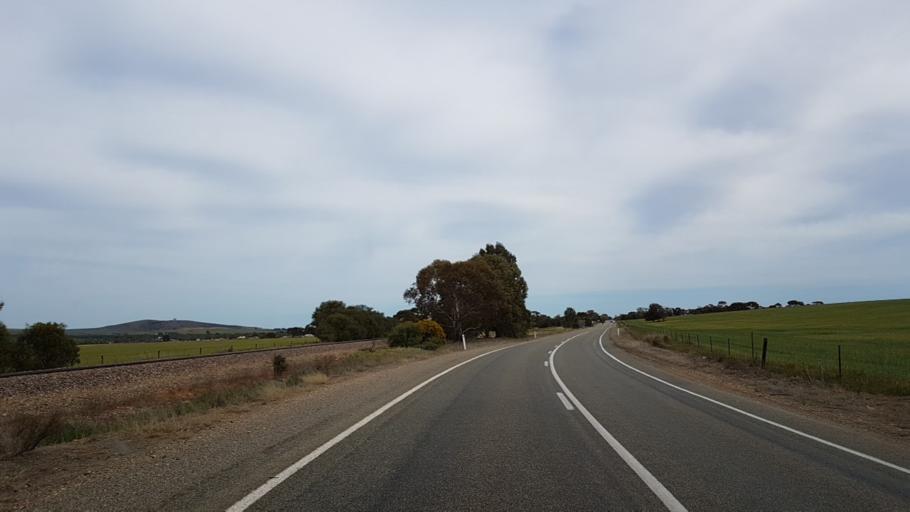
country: AU
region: South Australia
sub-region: Port Pirie City and Dists
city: Crystal Brook
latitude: -33.2508
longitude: 138.3650
